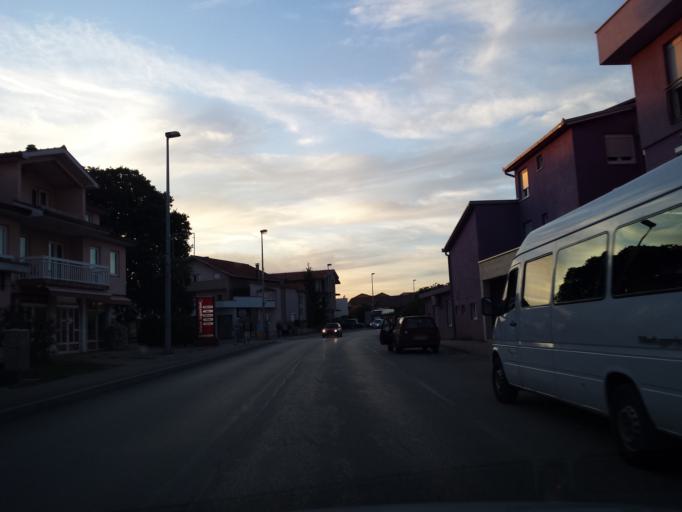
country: BA
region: Federation of Bosnia and Herzegovina
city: Citluk
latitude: 43.1964
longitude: 17.6745
